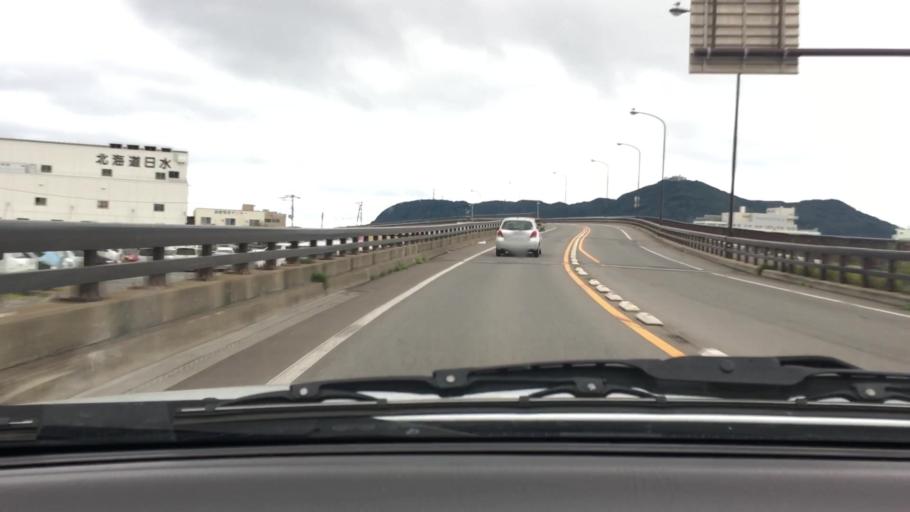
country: JP
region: Hokkaido
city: Hakodate
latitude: 41.7859
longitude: 140.7279
